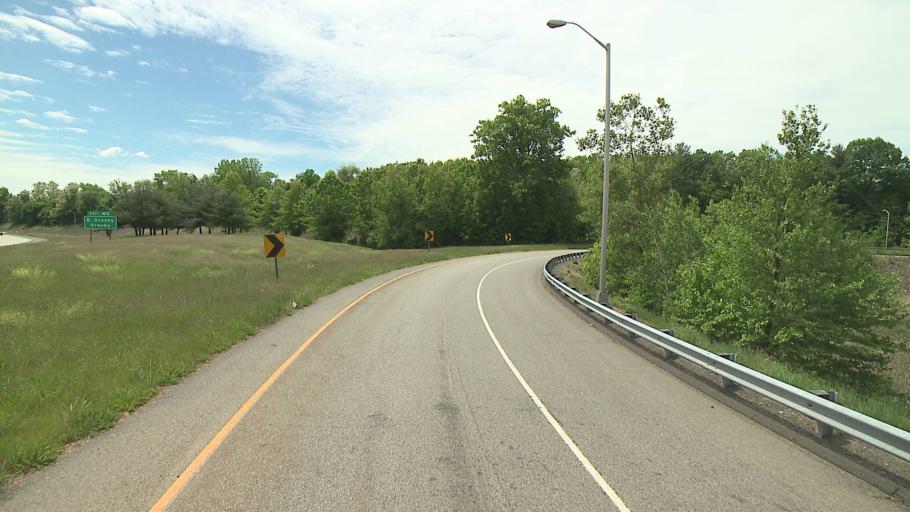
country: US
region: Connecticut
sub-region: Hartford County
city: Windsor Locks
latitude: 41.9154
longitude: -72.6290
